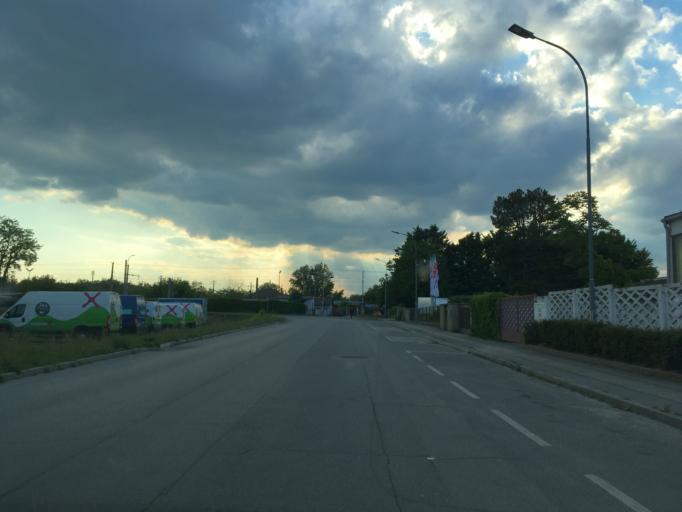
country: AT
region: Lower Austria
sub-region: Politischer Bezirk Wien-Umgebung
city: Gerasdorf bei Wien
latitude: 48.2820
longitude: 16.4807
